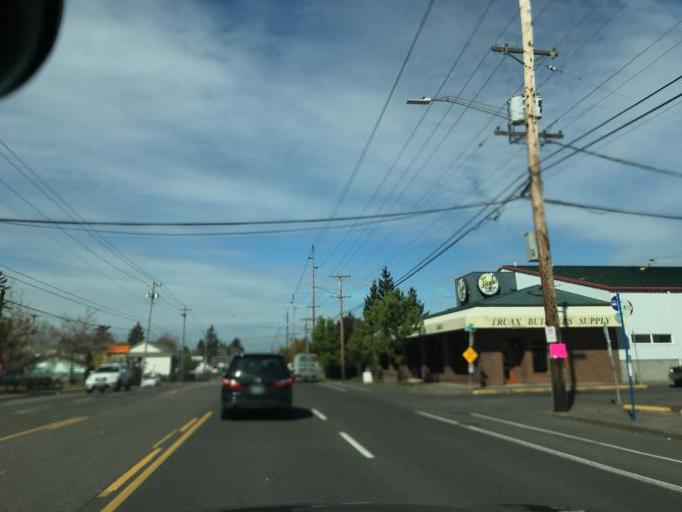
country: US
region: Oregon
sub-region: Multnomah County
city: Lents
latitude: 45.5042
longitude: -122.5499
